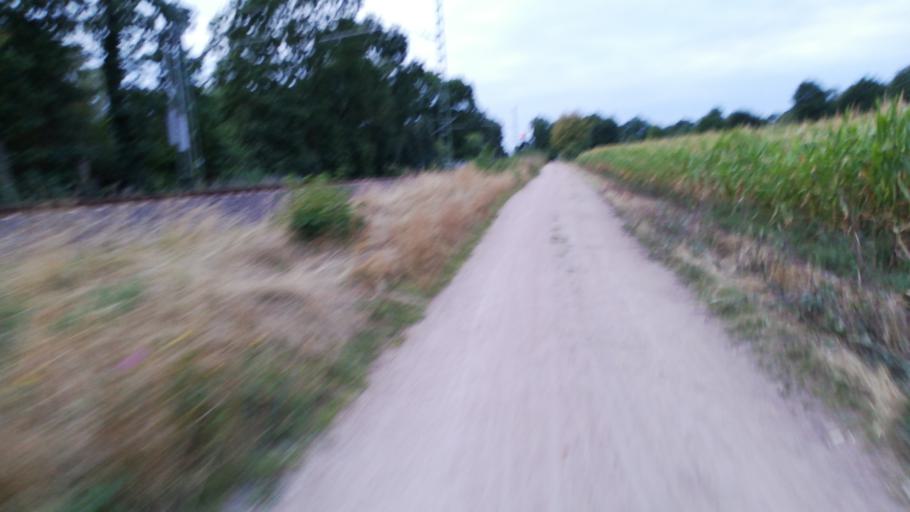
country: DE
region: Lower Saxony
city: Neu Wulmstorf
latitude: 53.4750
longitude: 9.8319
